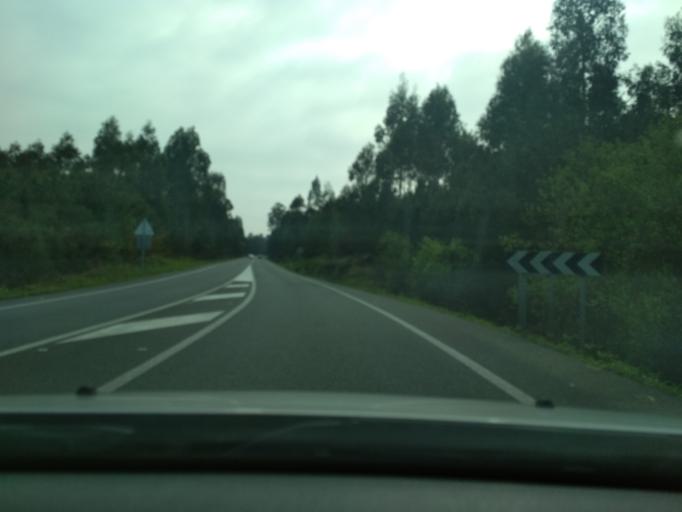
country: ES
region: Galicia
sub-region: Provincia de Pontevedra
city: Catoira
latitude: 42.6529
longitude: -8.7035
